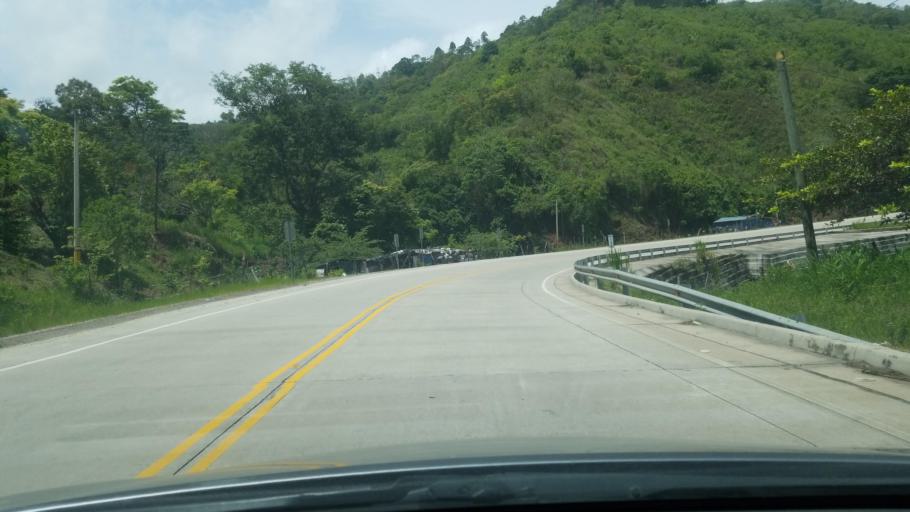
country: HN
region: Copan
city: Agua Caliente
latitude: 14.8564
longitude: -88.7966
